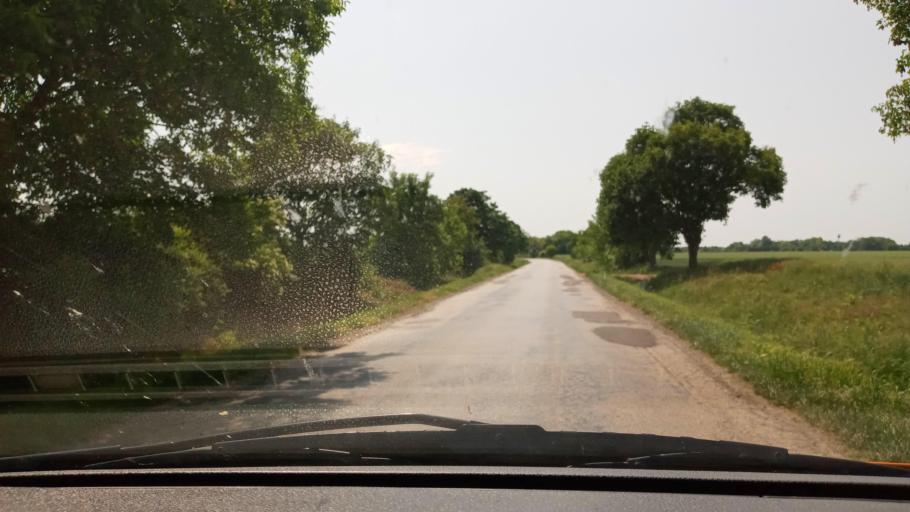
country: HU
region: Baranya
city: Szentlorinc
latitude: 46.0176
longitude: 18.0344
